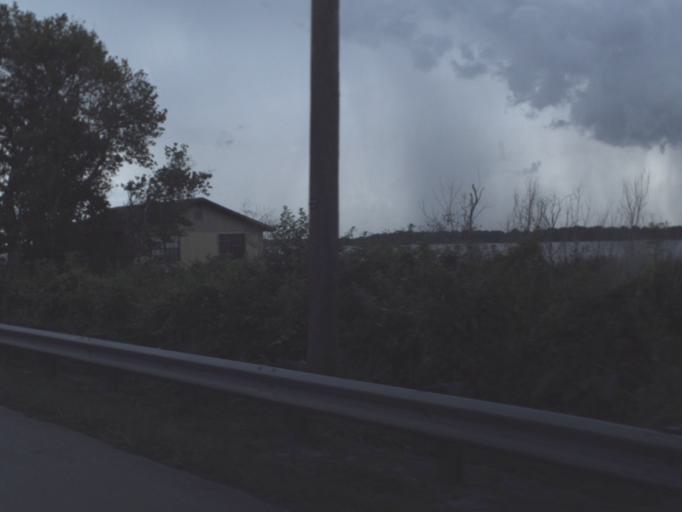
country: US
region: Florida
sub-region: Polk County
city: Polk City
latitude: 28.1354
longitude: -81.7950
